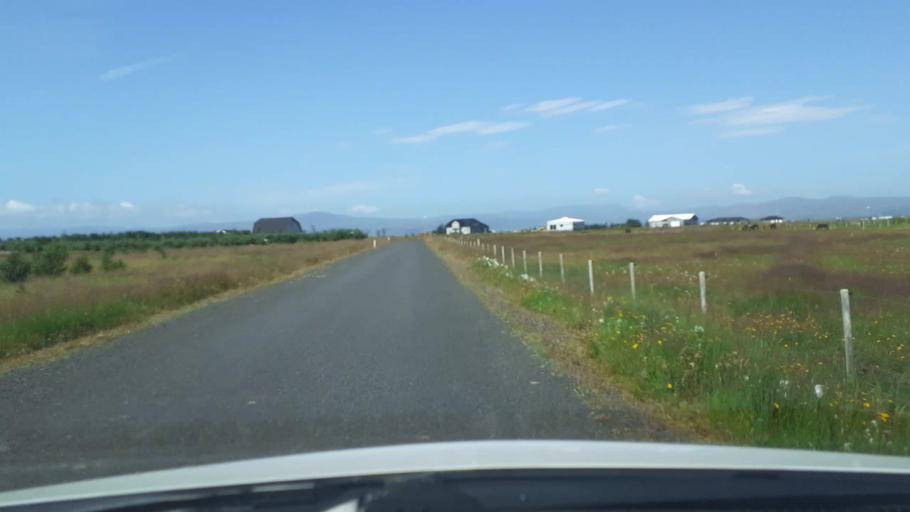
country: IS
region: South
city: Selfoss
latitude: 63.8906
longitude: -21.0852
